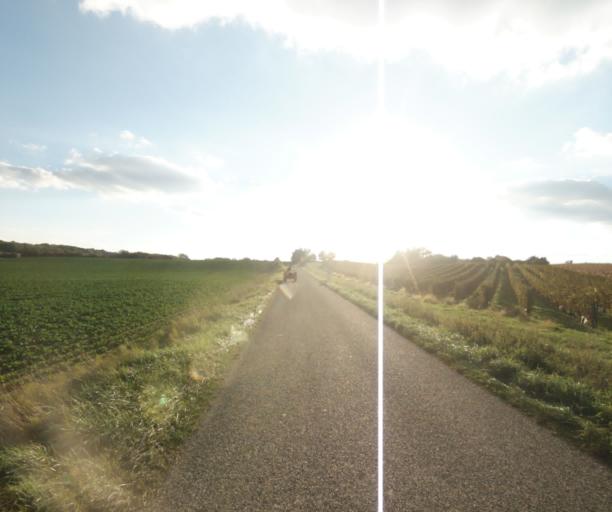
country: FR
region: Midi-Pyrenees
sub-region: Departement du Gers
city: Eauze
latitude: 43.7582
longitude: 0.1583
